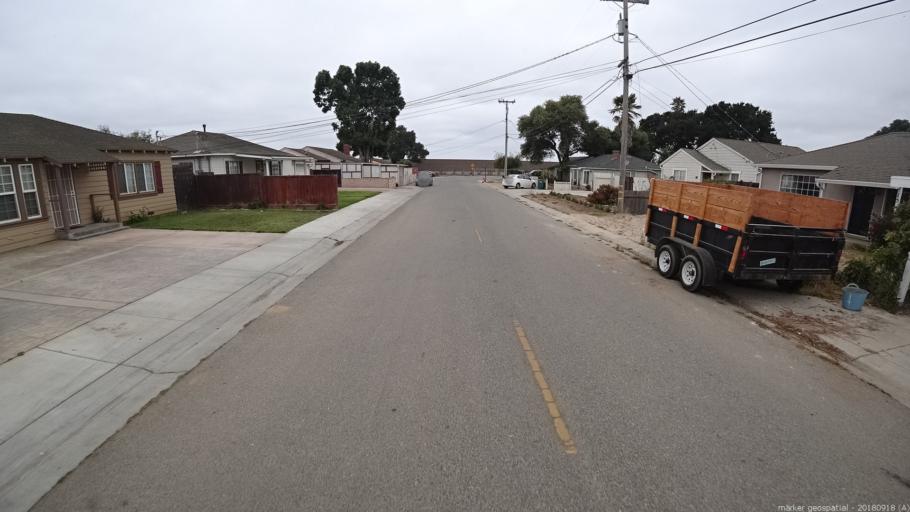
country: US
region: California
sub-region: Monterey County
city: Prunedale
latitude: 36.7489
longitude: -121.6611
